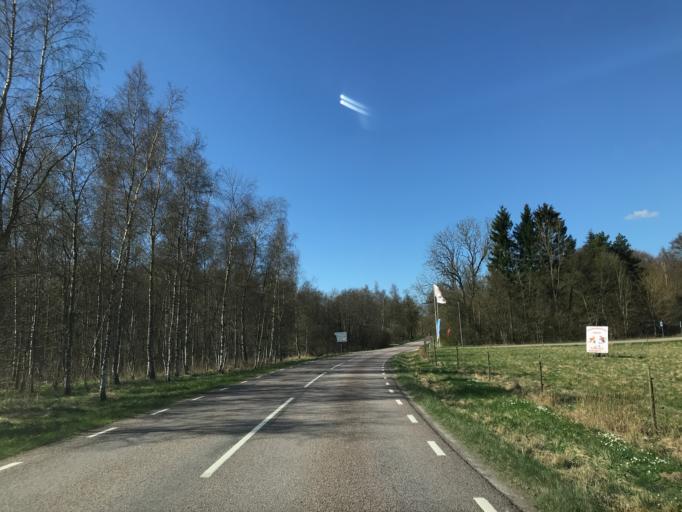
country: SE
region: Skane
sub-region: Svalovs Kommun
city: Kagerod
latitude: 55.9884
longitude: 13.1041
